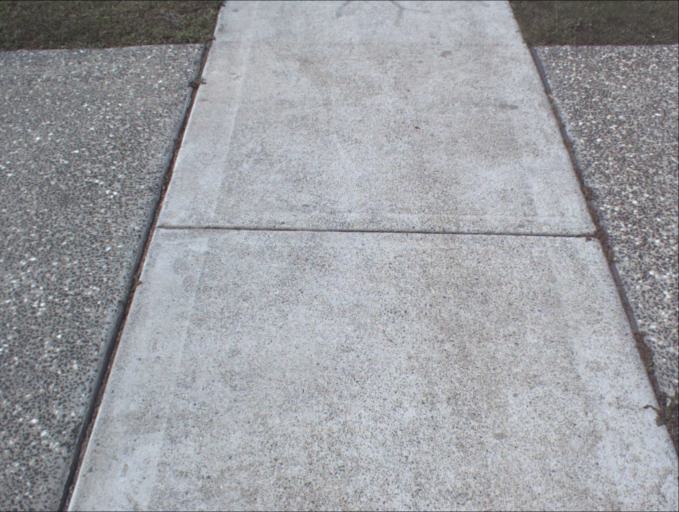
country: AU
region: Queensland
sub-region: Logan
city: Chambers Flat
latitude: -27.8063
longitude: 153.1085
